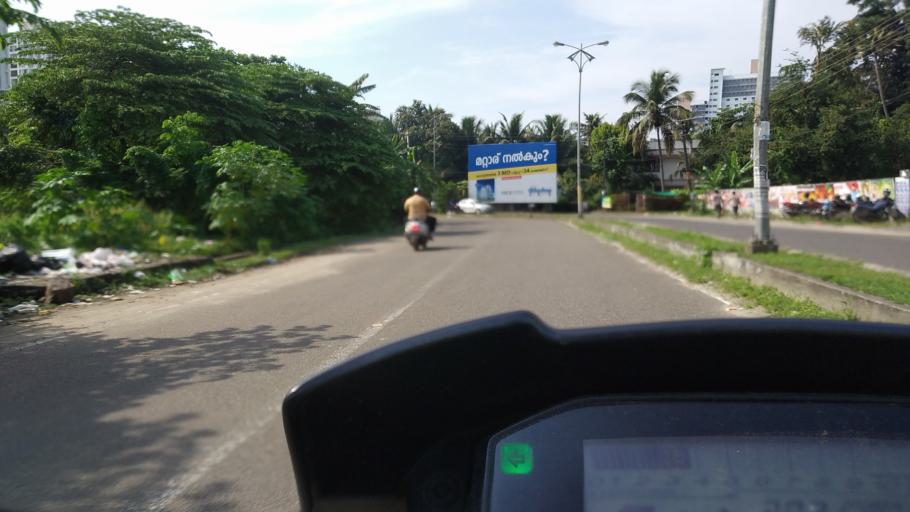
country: IN
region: Kerala
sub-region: Ernakulam
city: Cochin
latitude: 9.9854
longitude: 76.3036
